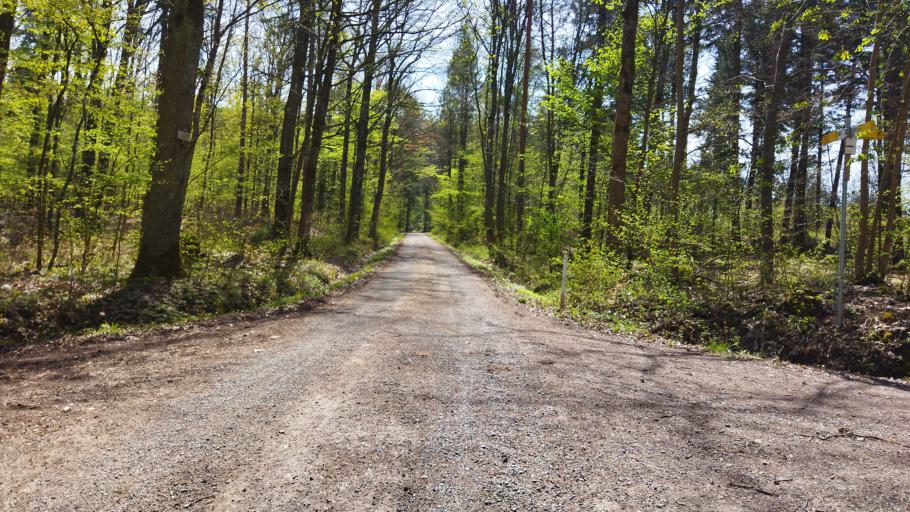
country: DE
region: Baden-Wuerttemberg
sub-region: Regierungsbezirk Stuttgart
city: Pfaffenhofen
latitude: 49.0477
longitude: 8.9587
